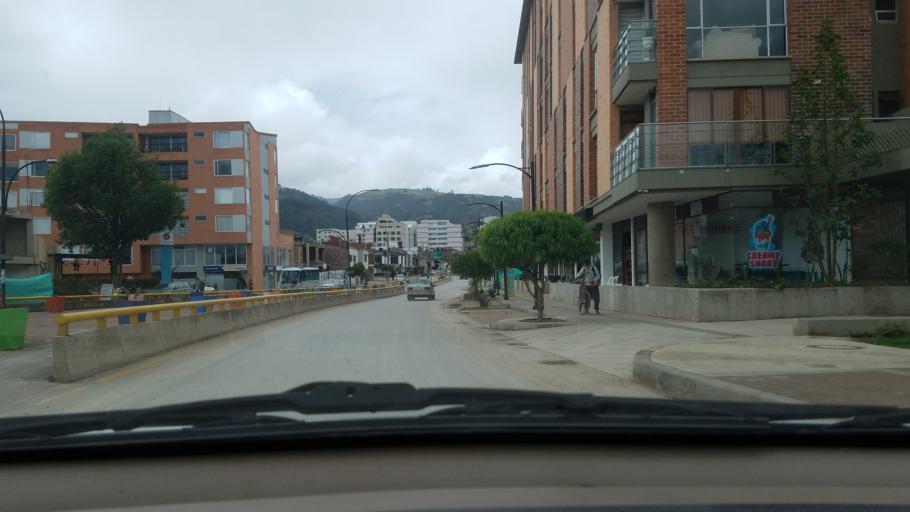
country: CO
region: Boyaca
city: Paipa
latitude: 5.7754
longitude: -73.1175
